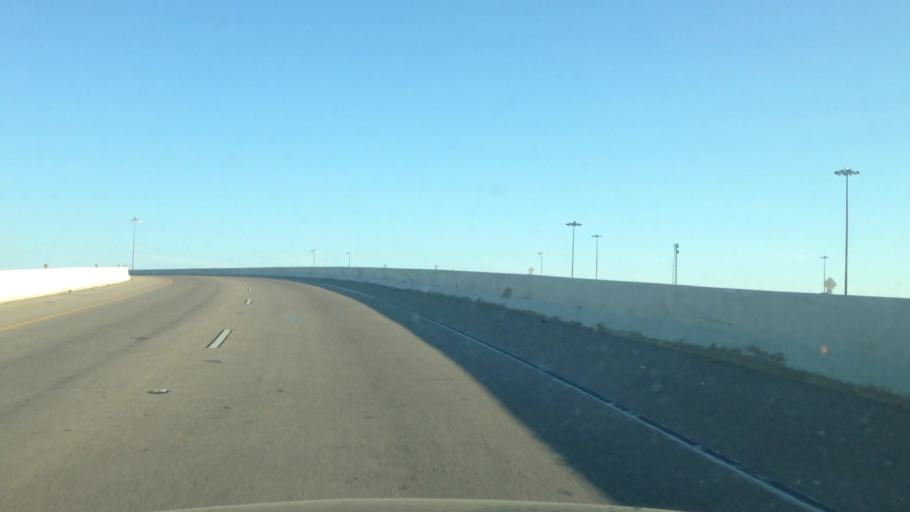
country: US
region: Texas
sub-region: Tarrant County
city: Fort Worth
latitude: 32.7491
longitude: -97.3203
